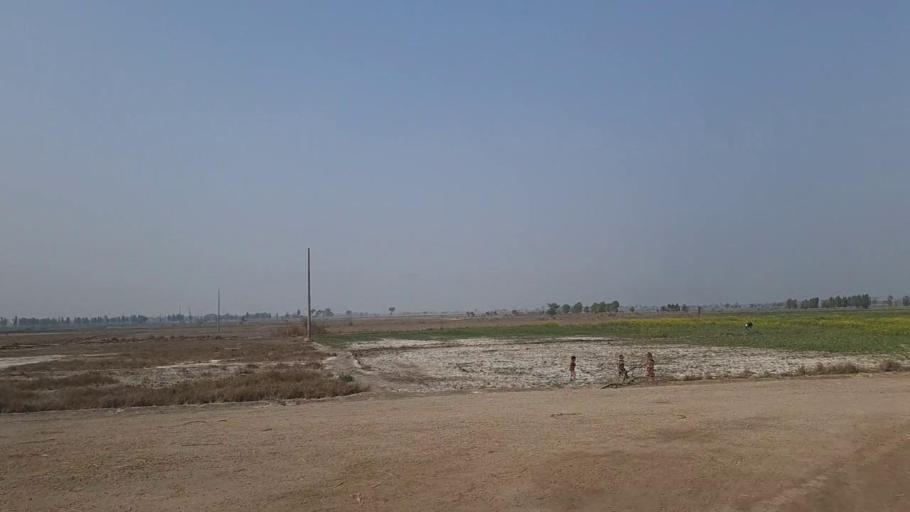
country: PK
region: Sindh
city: Daur
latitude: 26.4330
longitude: 68.4423
